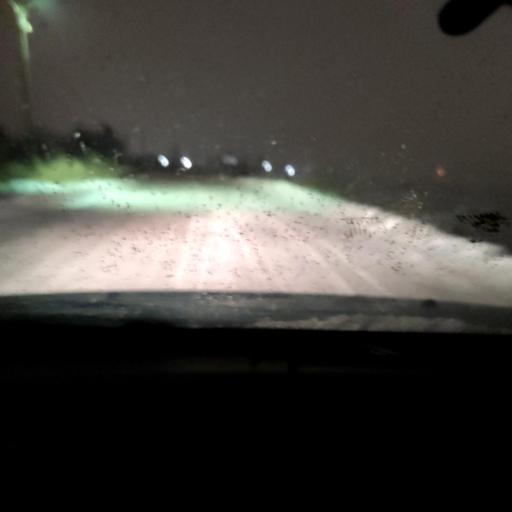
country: RU
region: Perm
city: Kondratovo
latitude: 58.0190
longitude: 56.1512
